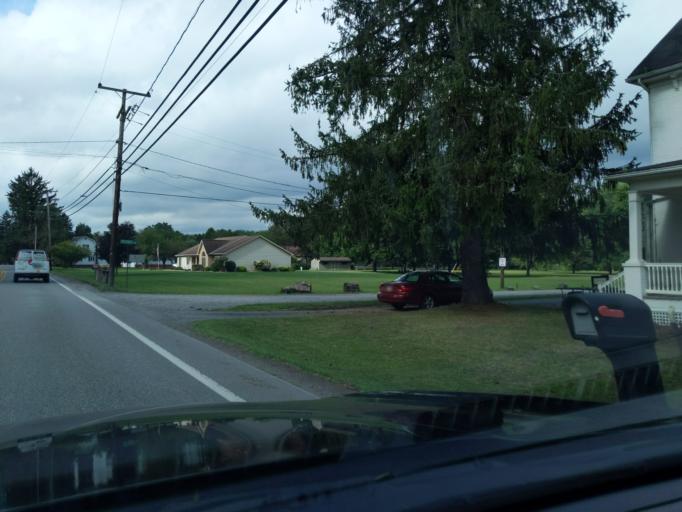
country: US
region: Pennsylvania
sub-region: Blair County
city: Roaring Spring
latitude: 40.3729
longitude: -78.4239
